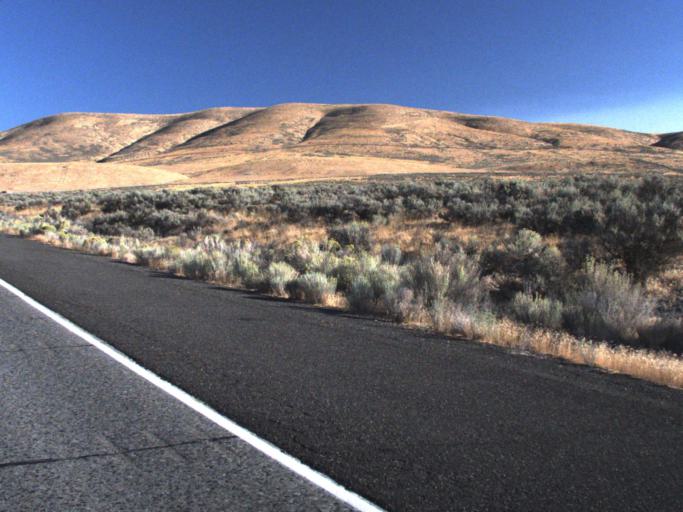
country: US
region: Washington
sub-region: Kittitas County
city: Kittitas
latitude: 46.8333
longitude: -120.3680
